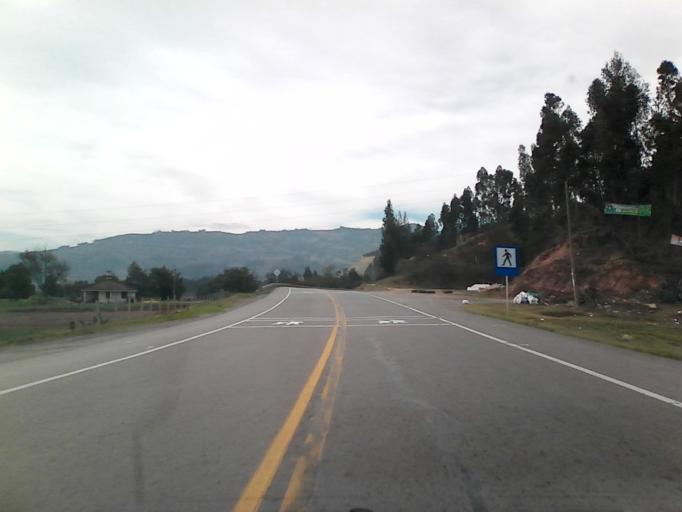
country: CO
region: Boyaca
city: Tibasosa
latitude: 5.7688
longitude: -72.9962
